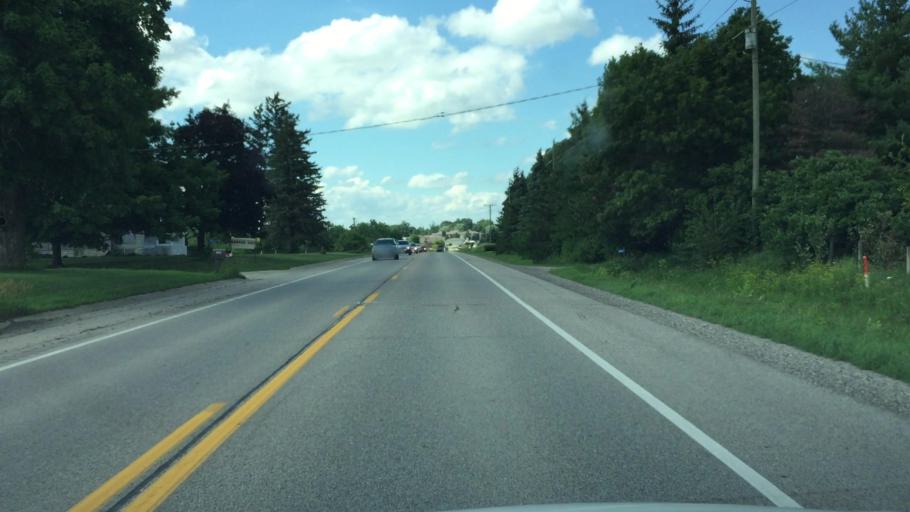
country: US
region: Iowa
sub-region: Johnson County
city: Solon
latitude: 41.7911
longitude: -91.4886
